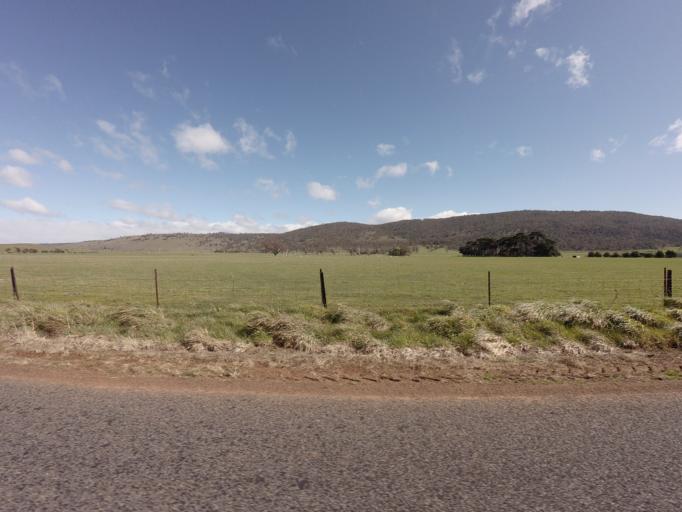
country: AU
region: Tasmania
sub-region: Northern Midlands
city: Evandale
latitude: -41.9845
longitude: 147.4502
